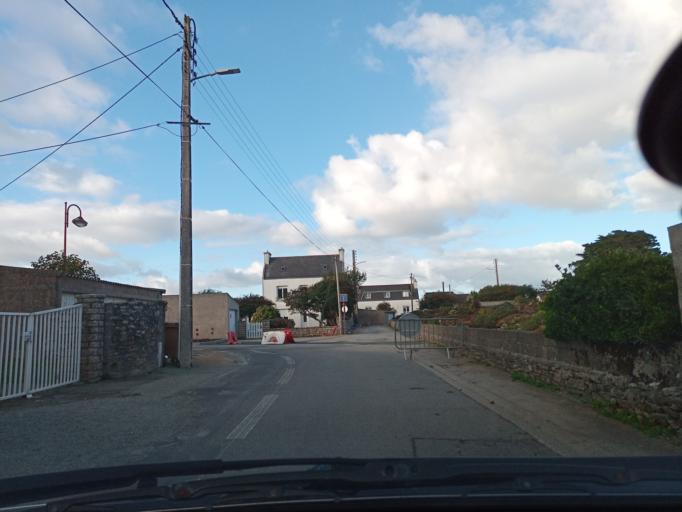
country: FR
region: Brittany
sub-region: Departement du Finistere
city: Plouhinec
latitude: 48.0158
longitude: -4.4907
